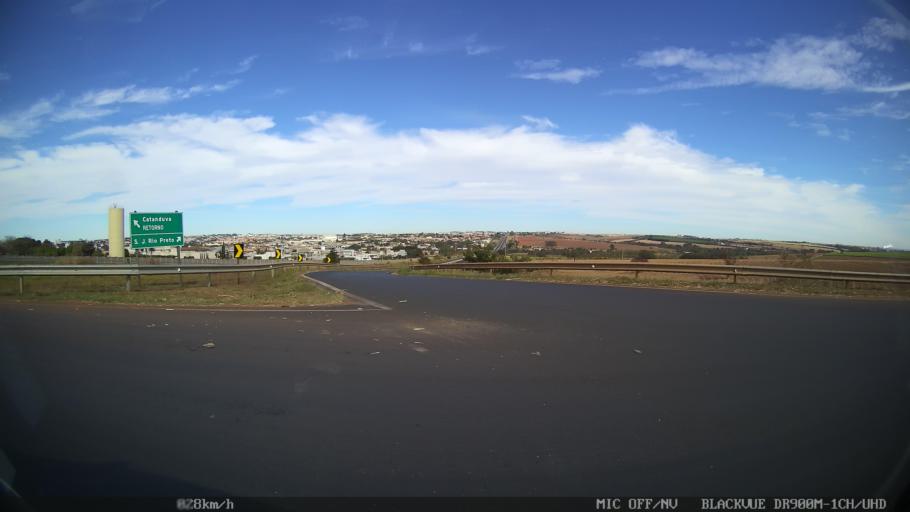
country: BR
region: Sao Paulo
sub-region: Catanduva
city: Catanduva
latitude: -21.1155
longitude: -48.9791
